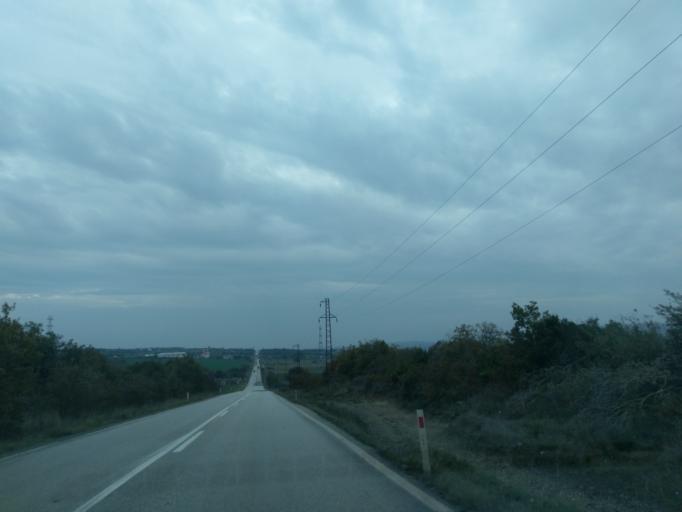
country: TR
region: Istanbul
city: Canta
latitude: 41.1530
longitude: 28.1068
